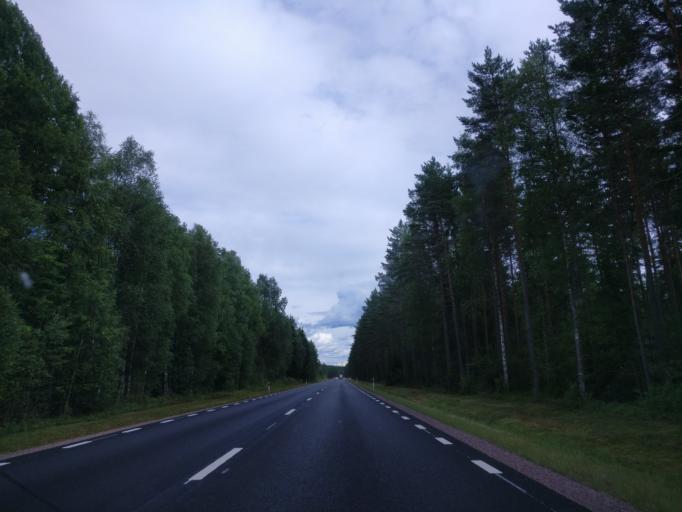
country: SE
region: Vaermland
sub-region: Hagfors Kommun
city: Hagfors
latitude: 60.0514
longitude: 13.5639
